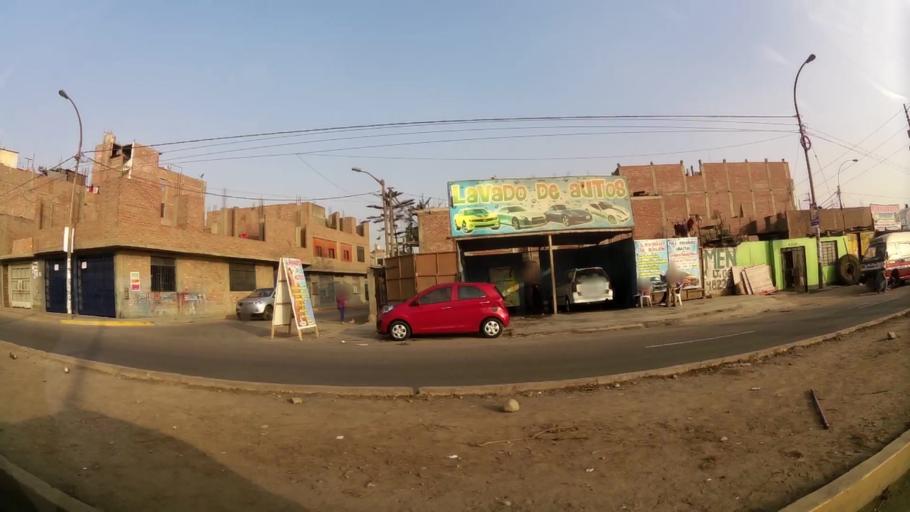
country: PE
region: Lima
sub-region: Lima
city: Independencia
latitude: -11.9475
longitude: -77.0766
